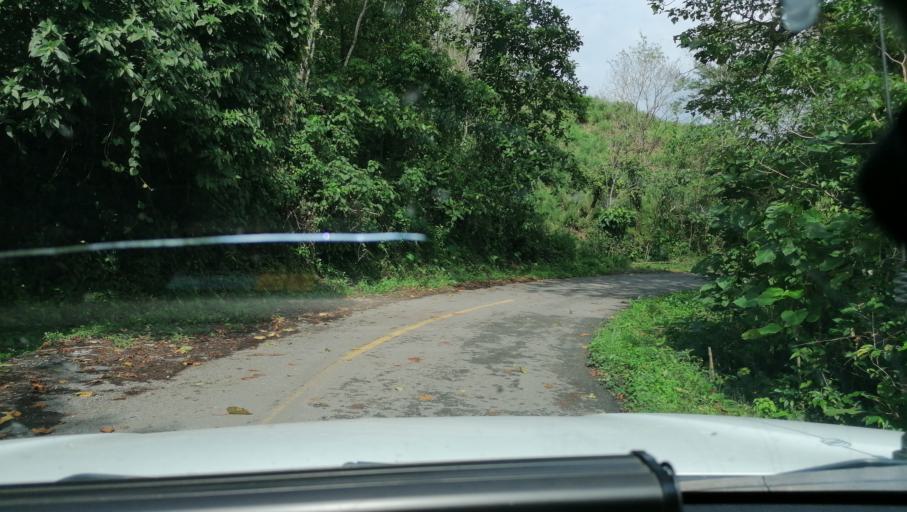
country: MX
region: Chiapas
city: Ocotepec
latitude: 17.3102
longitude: -93.1796
